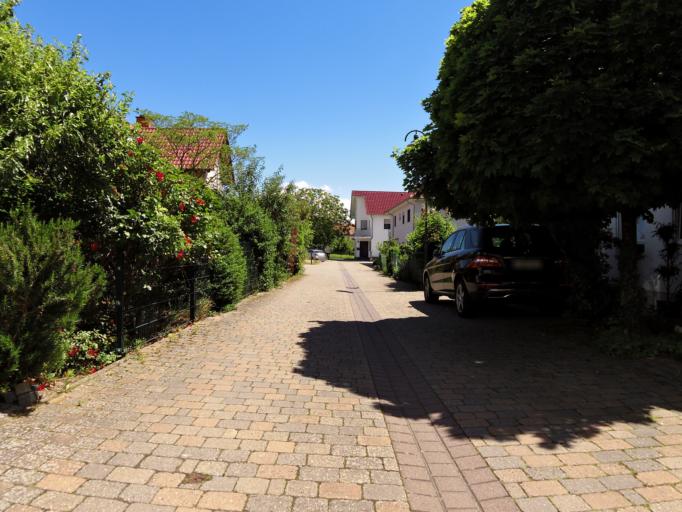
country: DE
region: Rheinland-Pfalz
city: Hainfeld
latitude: 49.2587
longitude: 8.0959
